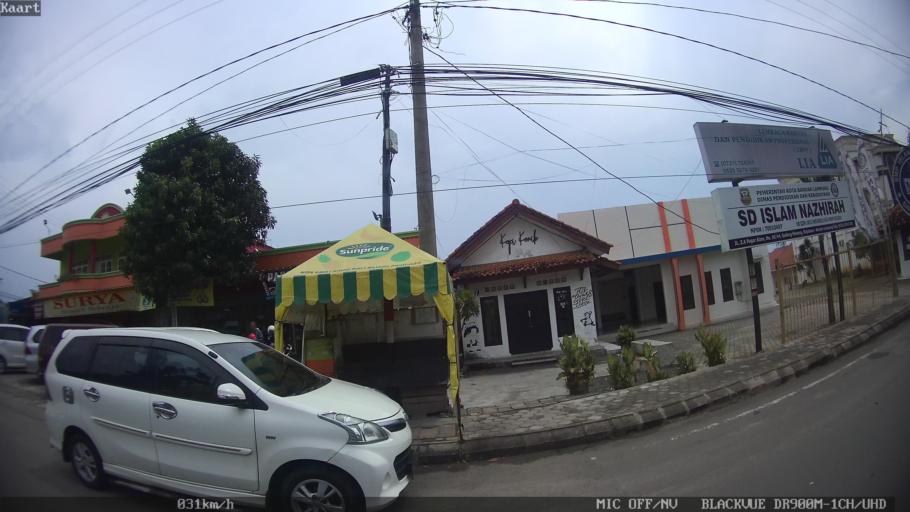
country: ID
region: Lampung
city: Kedaton
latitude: -5.3745
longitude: 105.2434
